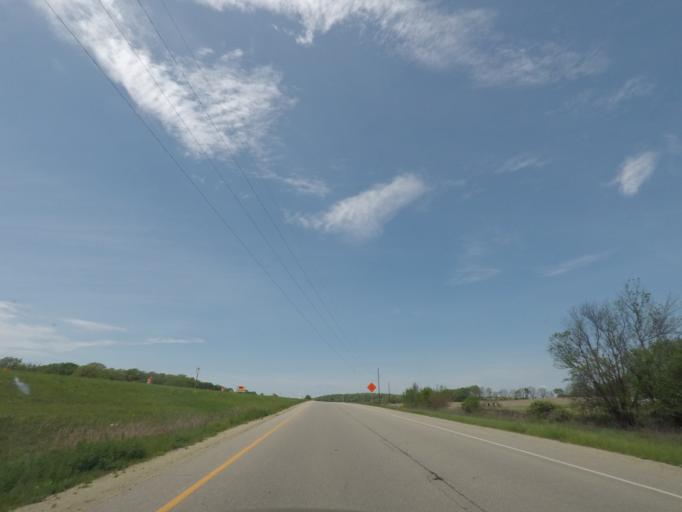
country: US
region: Wisconsin
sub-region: Dane County
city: Oregon
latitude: 42.9533
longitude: -89.3792
